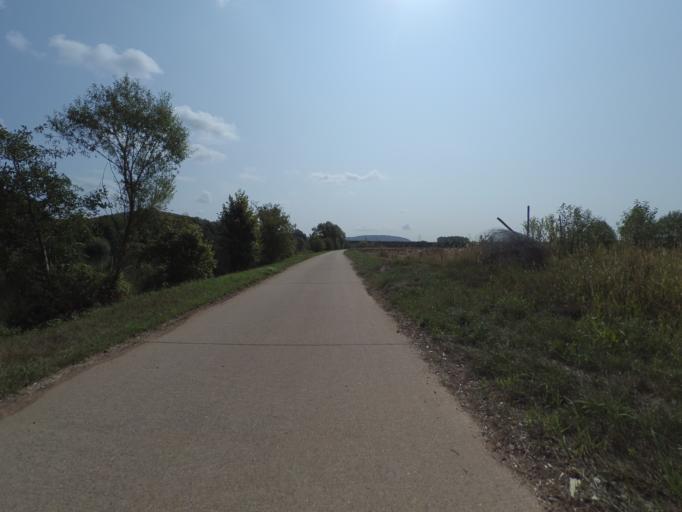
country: DE
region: Saarland
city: Mettlach
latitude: 49.4661
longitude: 6.6098
